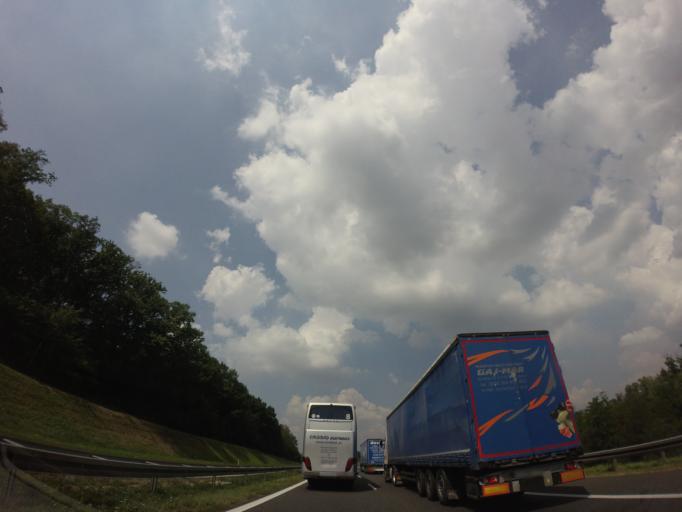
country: PL
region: Silesian Voivodeship
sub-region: Powiat gliwicki
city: Rudziniec
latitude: 50.3841
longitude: 18.4608
